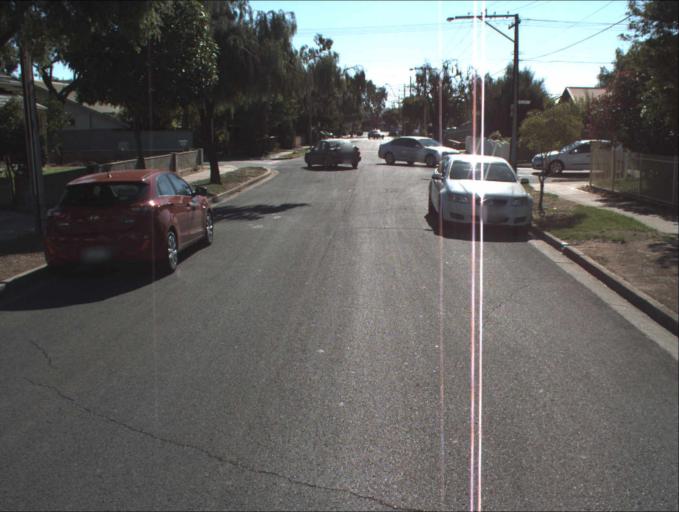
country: AU
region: South Australia
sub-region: Prospect
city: Prospect
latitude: -34.8754
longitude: 138.6054
